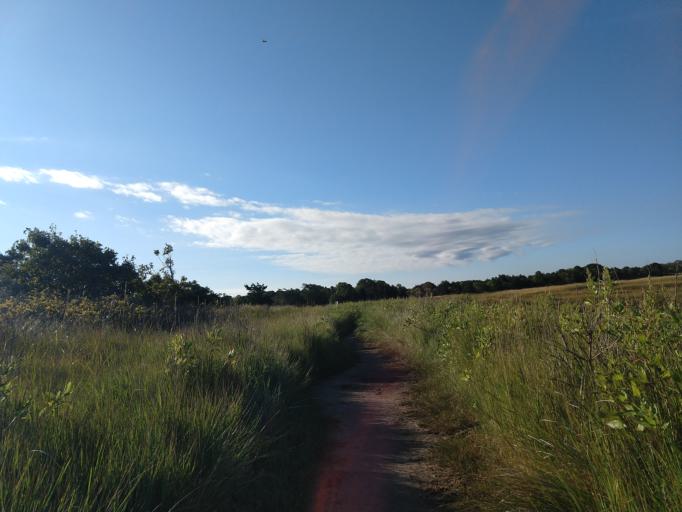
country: US
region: Massachusetts
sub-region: Barnstable County
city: North Eastham
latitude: 41.8820
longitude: -70.0016
